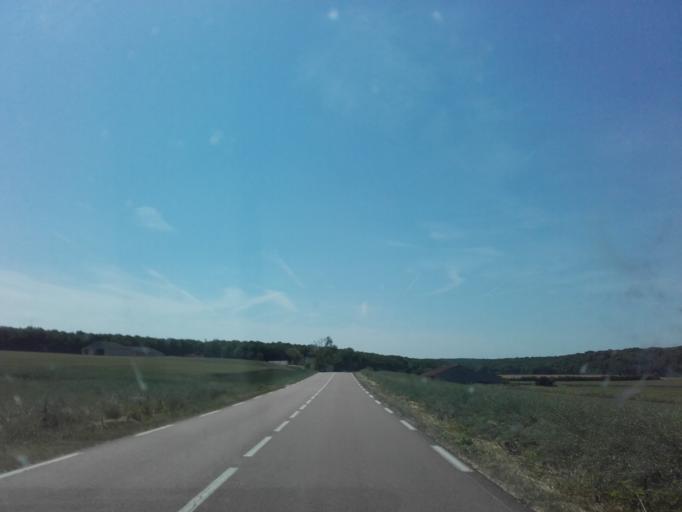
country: FR
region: Bourgogne
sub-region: Departement de l'Yonne
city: Chablis
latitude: 47.7620
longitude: 3.8191
